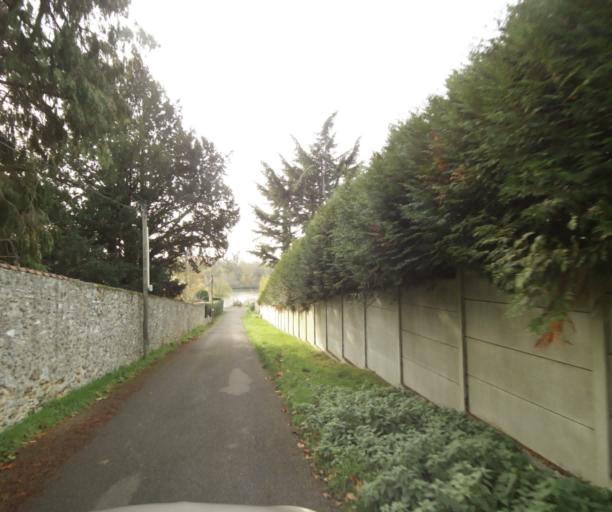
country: FR
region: Ile-de-France
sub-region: Departement des Yvelines
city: Triel-sur-Seine
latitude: 48.9896
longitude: 1.9922
